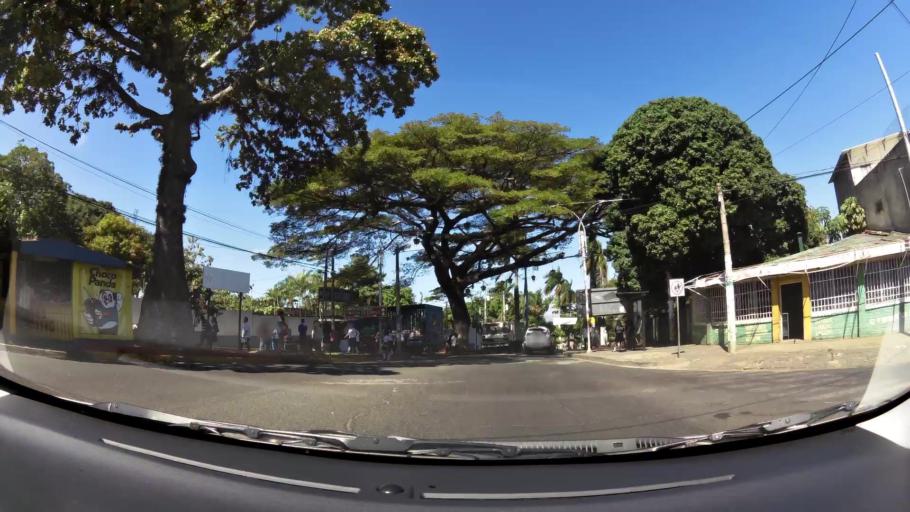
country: SV
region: Ahuachapan
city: Ahuachapan
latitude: 13.9248
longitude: -89.8501
